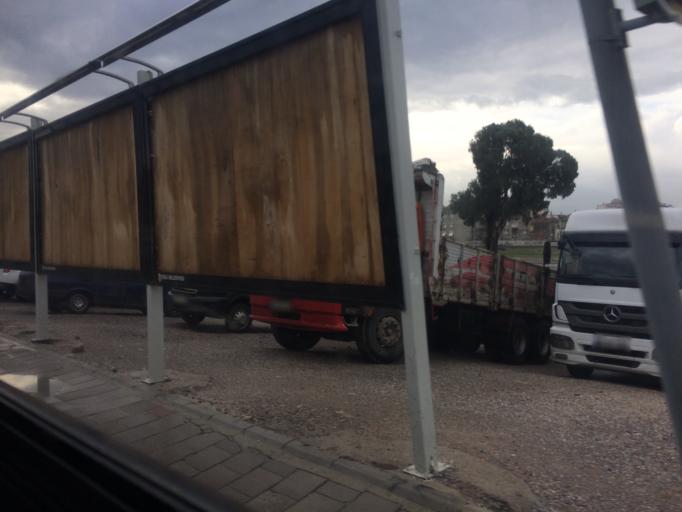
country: TR
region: Izmir
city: Karsiyaka
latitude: 38.4963
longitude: 27.0595
